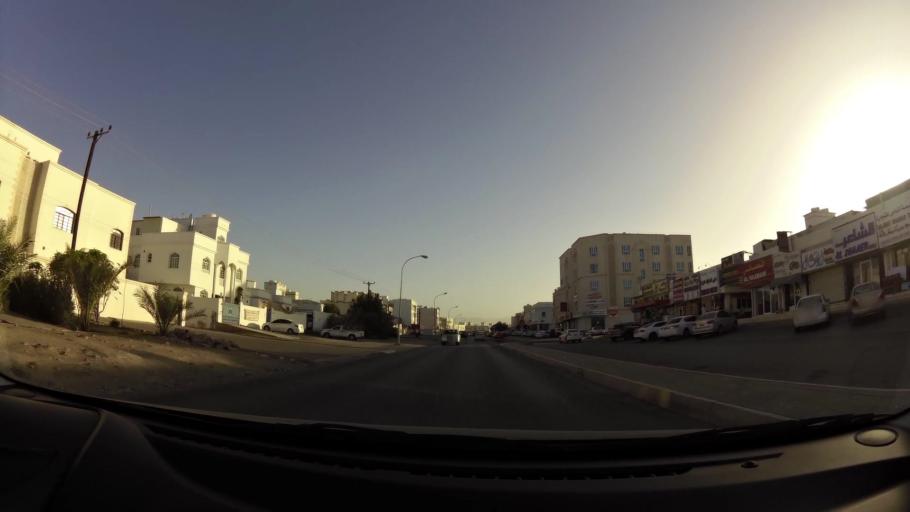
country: OM
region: Muhafazat Masqat
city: As Sib al Jadidah
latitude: 23.6060
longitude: 58.2264
